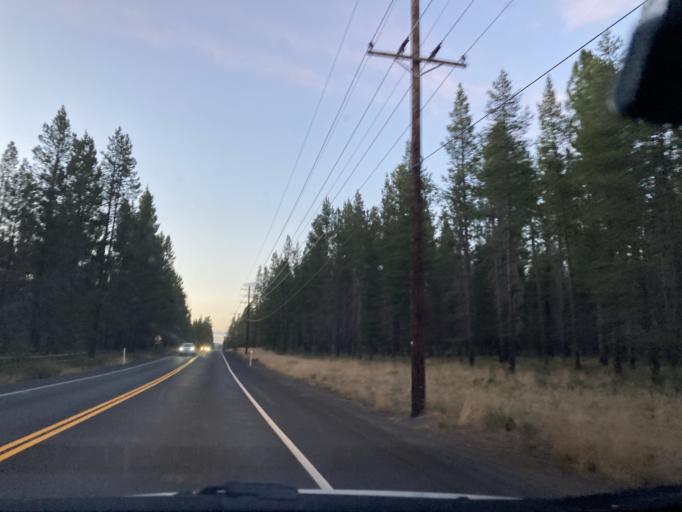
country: US
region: Oregon
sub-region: Deschutes County
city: Three Rivers
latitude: 43.8363
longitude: -121.4419
